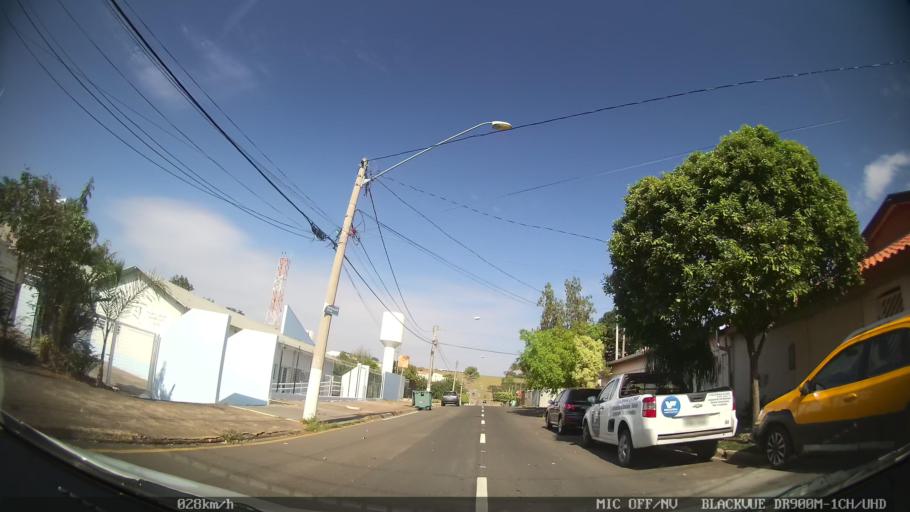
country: BR
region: Sao Paulo
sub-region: Paulinia
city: Paulinia
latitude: -22.7772
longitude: -47.1658
